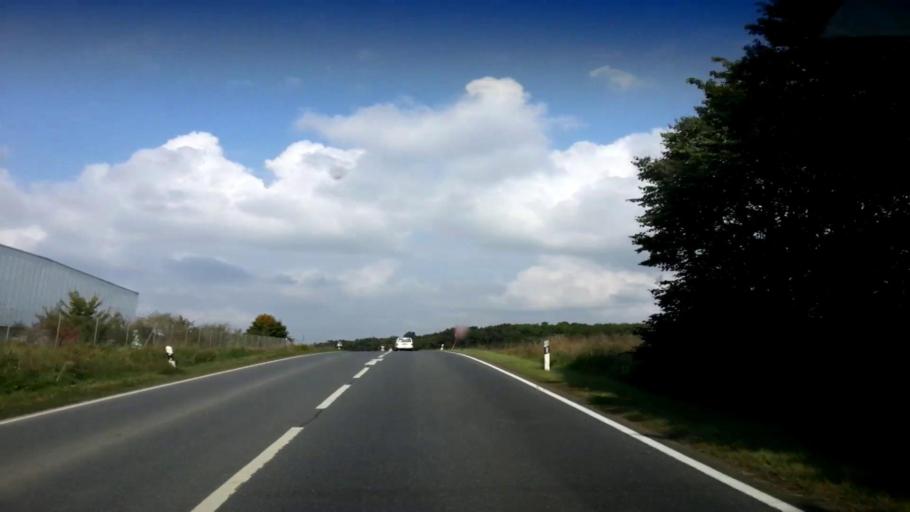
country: DE
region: Bavaria
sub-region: Regierungsbezirk Unterfranken
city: Wiesentheid
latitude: 49.7789
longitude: 10.3424
